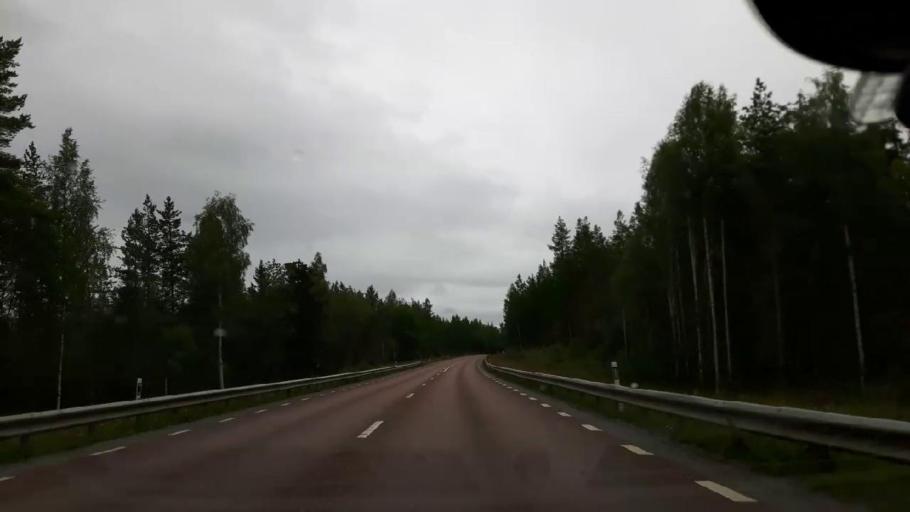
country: SE
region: Jaemtland
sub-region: Bergs Kommun
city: Hoverberg
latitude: 62.8209
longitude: 14.5164
